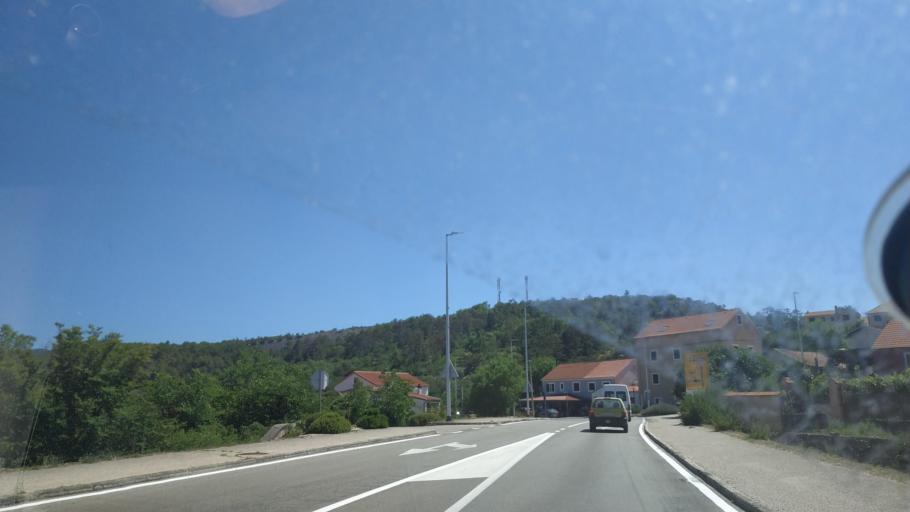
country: HR
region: Sibensko-Kniniska
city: Drnis
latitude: 43.8583
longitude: 16.1590
